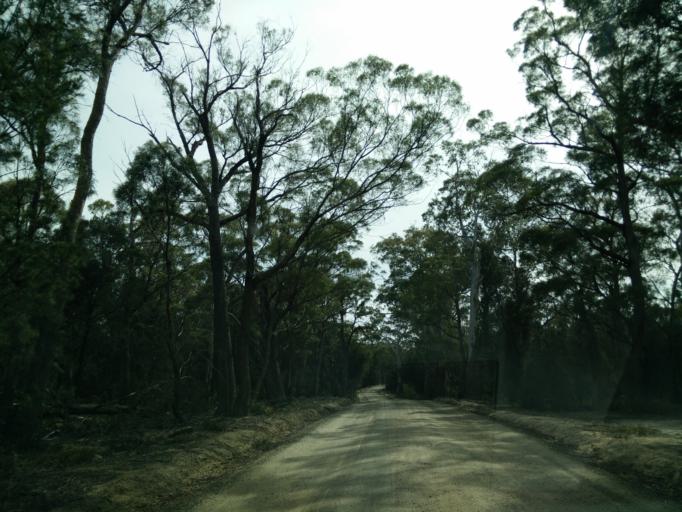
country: AU
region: Tasmania
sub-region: Break O'Day
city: St Helens
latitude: -41.9981
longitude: 148.2744
